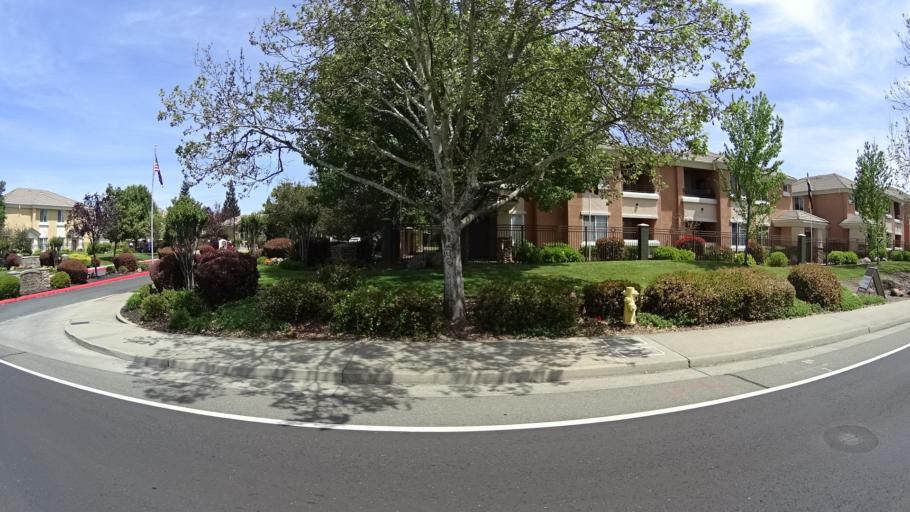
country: US
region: California
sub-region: Placer County
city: Rocklin
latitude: 38.7999
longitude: -121.2688
